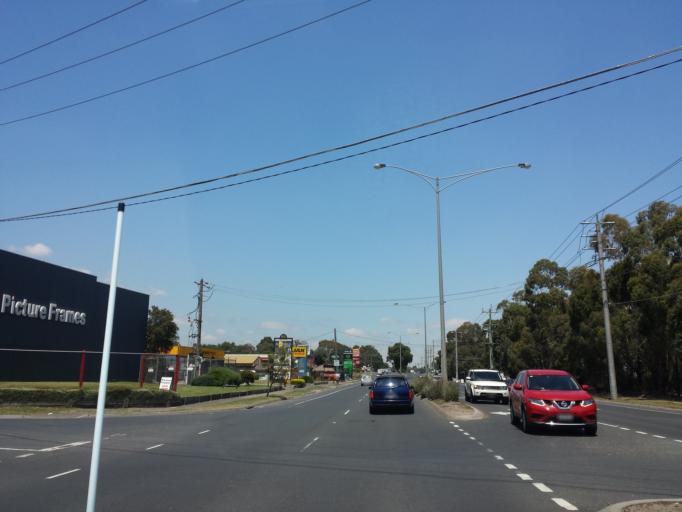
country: AU
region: Victoria
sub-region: Maroondah
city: Bayswater North
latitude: -37.8223
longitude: 145.2878
